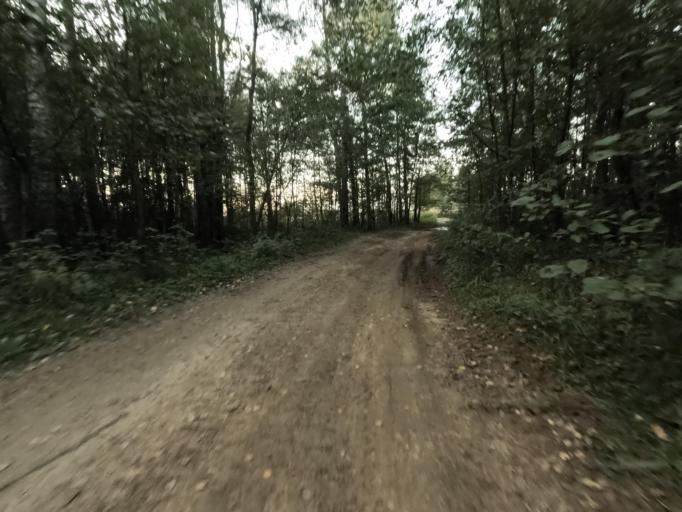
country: RU
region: Leningrad
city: Otradnoye
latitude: 59.8533
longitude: 30.7949
